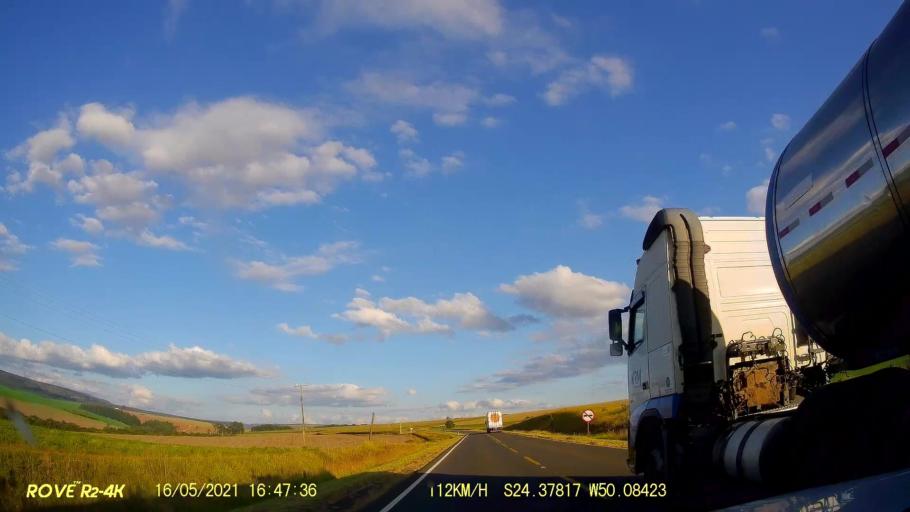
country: BR
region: Parana
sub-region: Pirai Do Sul
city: Pirai do Sul
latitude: -24.3782
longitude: -50.0839
